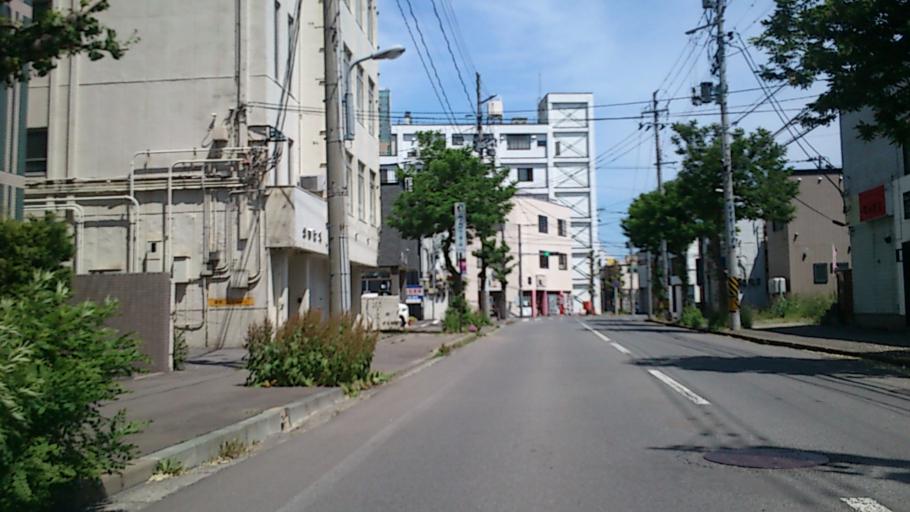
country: JP
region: Aomori
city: Aomori Shi
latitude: 40.8272
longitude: 140.7430
